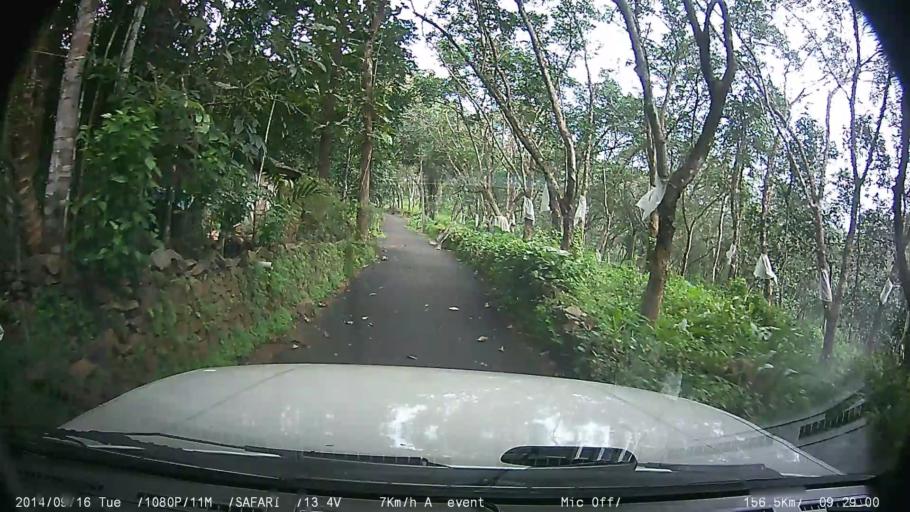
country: IN
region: Kerala
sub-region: Kottayam
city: Palackattumala
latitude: 9.7768
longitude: 76.5587
